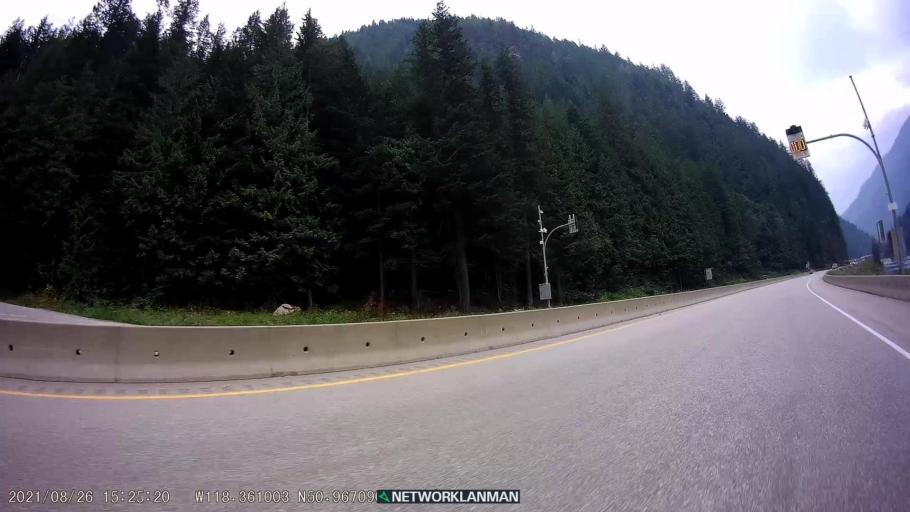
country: CA
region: British Columbia
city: Revelstoke
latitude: 50.9673
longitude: -118.3613
